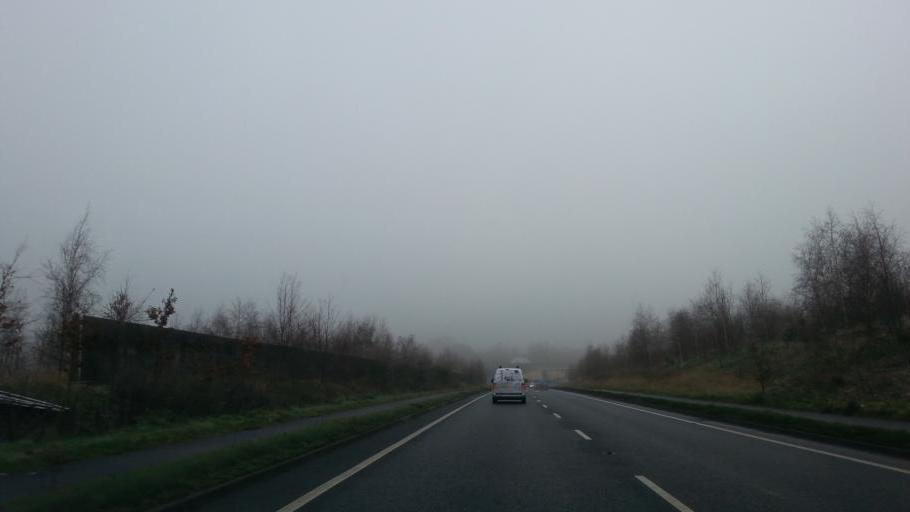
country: GB
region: England
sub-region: Cheshire East
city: Alderley Edge
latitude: 53.3045
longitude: -2.2469
